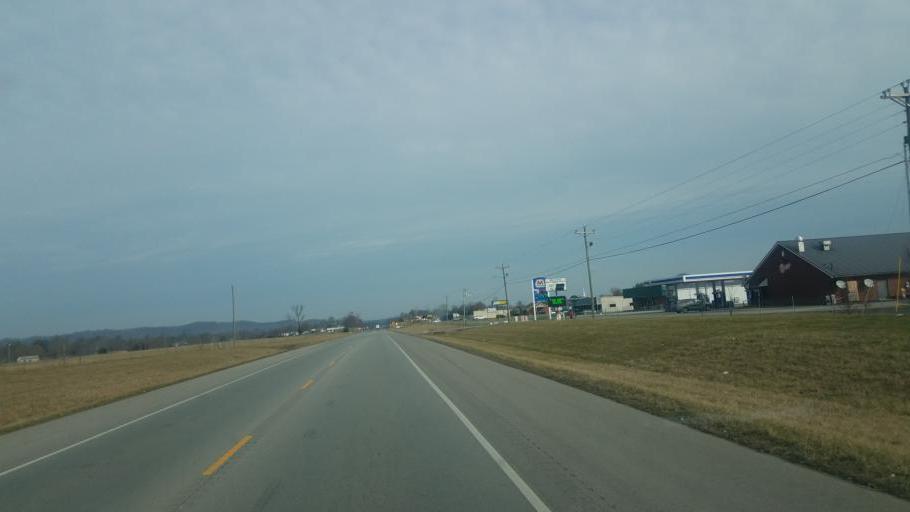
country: US
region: Kentucky
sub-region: Boyle County
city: Junction City
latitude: 37.5149
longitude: -84.8066
